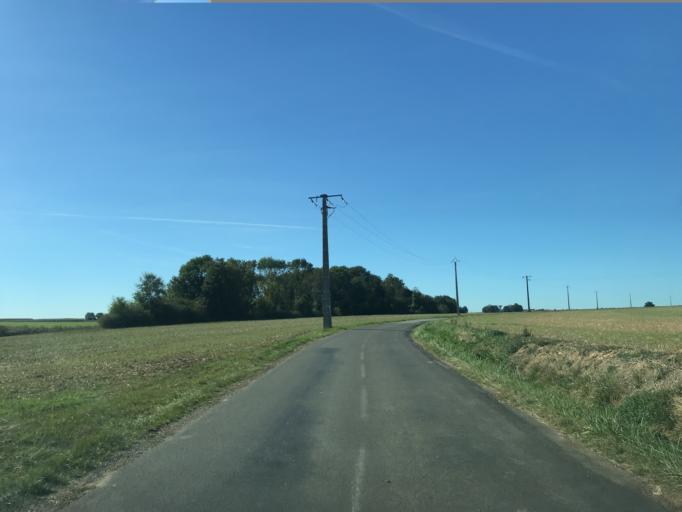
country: FR
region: Haute-Normandie
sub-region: Departement de l'Eure
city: Ande
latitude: 49.1750
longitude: 1.2584
